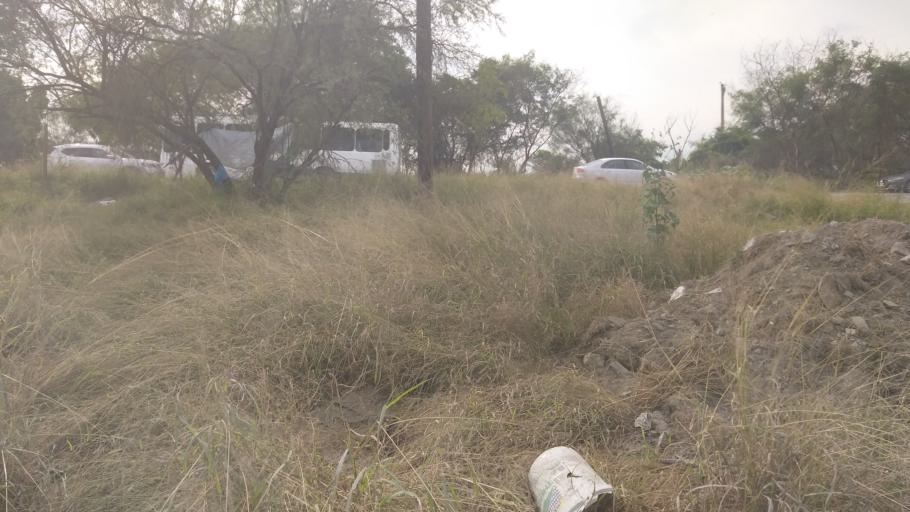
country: MX
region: Nuevo Leon
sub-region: Apodaca
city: Loma la Paz
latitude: 25.7027
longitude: -100.1453
